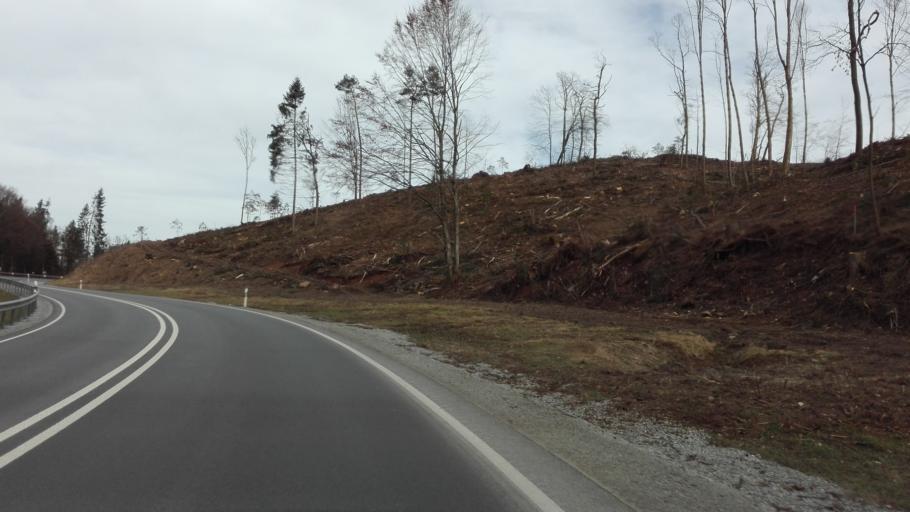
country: DE
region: Bavaria
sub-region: Lower Bavaria
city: Thyrnau
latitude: 48.6299
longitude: 13.5765
